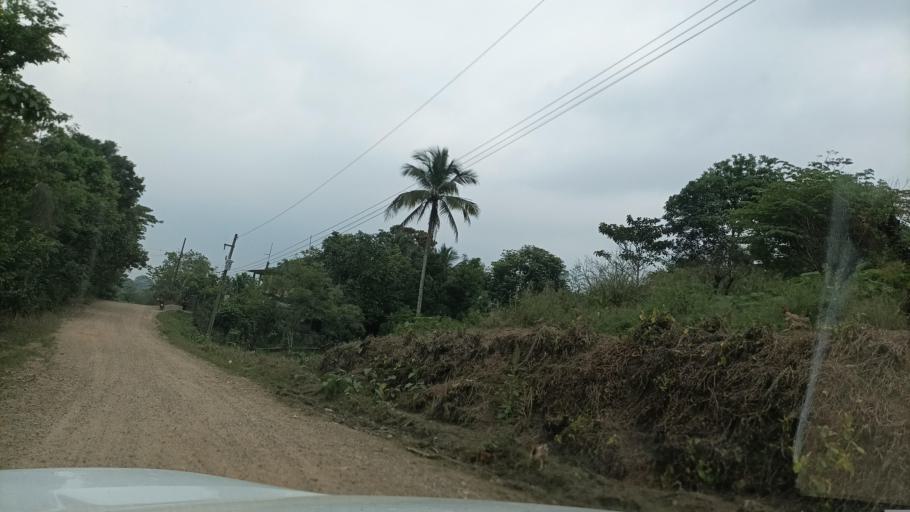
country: MX
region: Veracruz
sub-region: Moloacan
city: Cuichapa
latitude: 17.5793
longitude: -94.2268
